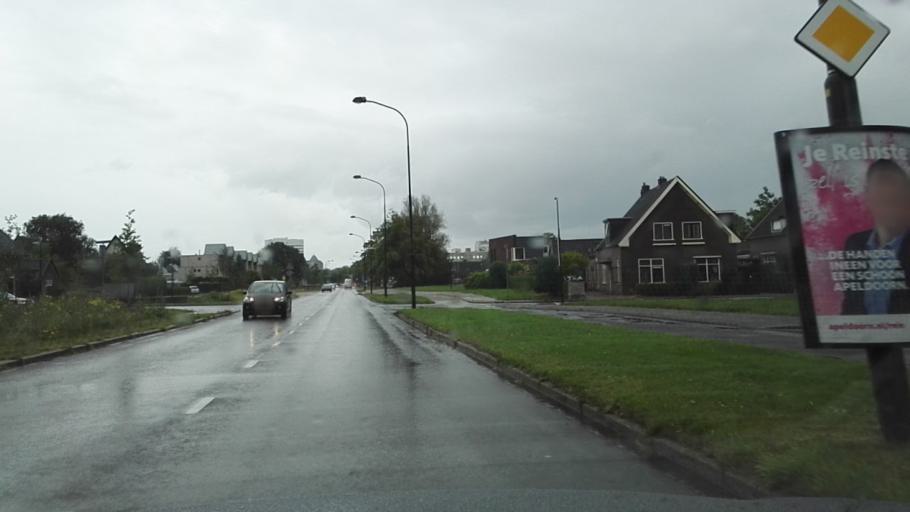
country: NL
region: Gelderland
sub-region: Gemeente Apeldoorn
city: Apeldoorn
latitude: 52.2075
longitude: 5.9519
